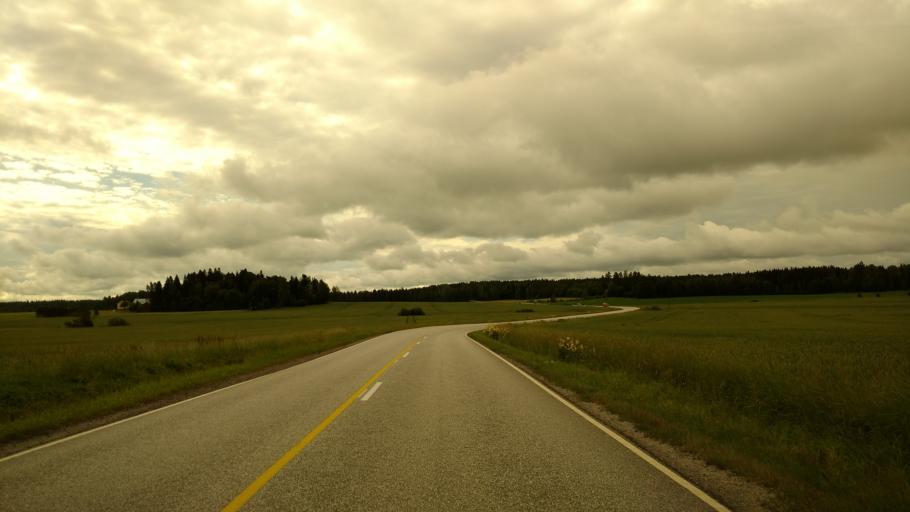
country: FI
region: Varsinais-Suomi
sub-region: Salo
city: Kuusjoki
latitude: 60.4638
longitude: 23.1632
